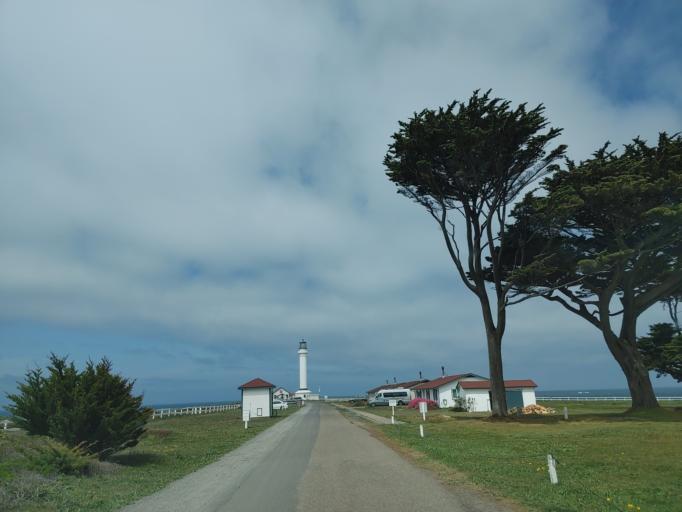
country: US
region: California
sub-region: Sonoma County
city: Sea Ranch
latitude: 38.9529
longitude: -123.7380
